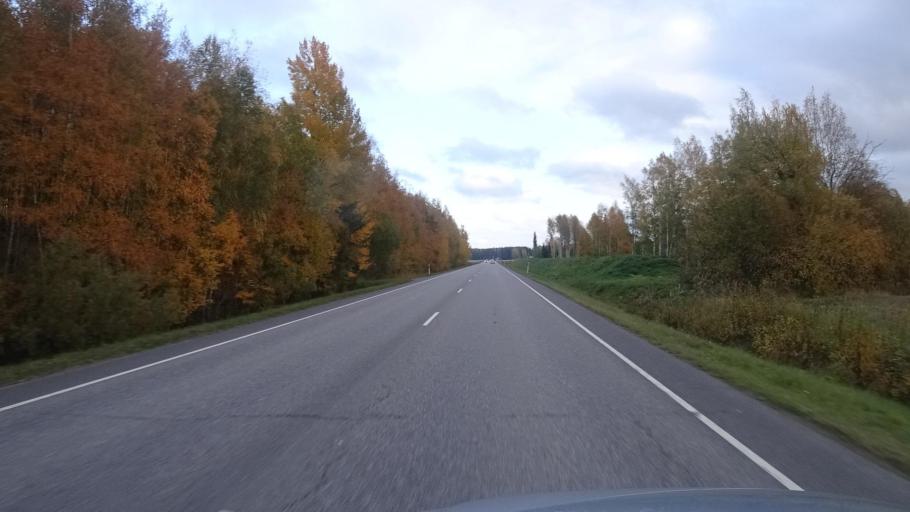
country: FI
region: Satakunta
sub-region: Rauma
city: Saekylae
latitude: 61.0433
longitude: 22.3709
